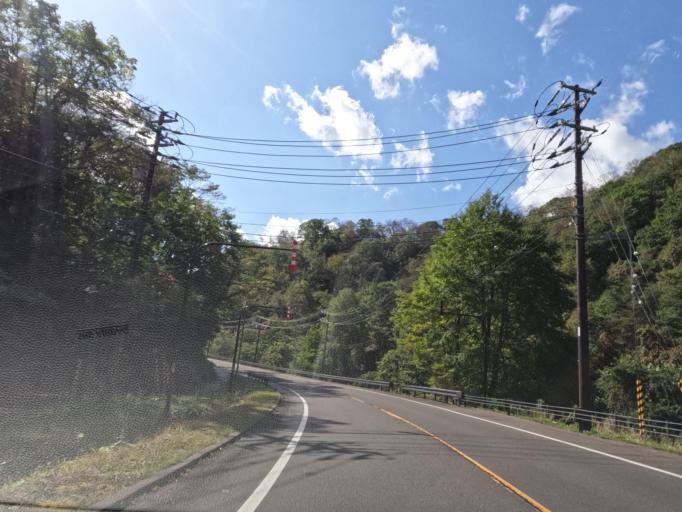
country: JP
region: Hokkaido
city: Shiraoi
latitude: 42.4855
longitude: 141.1451
